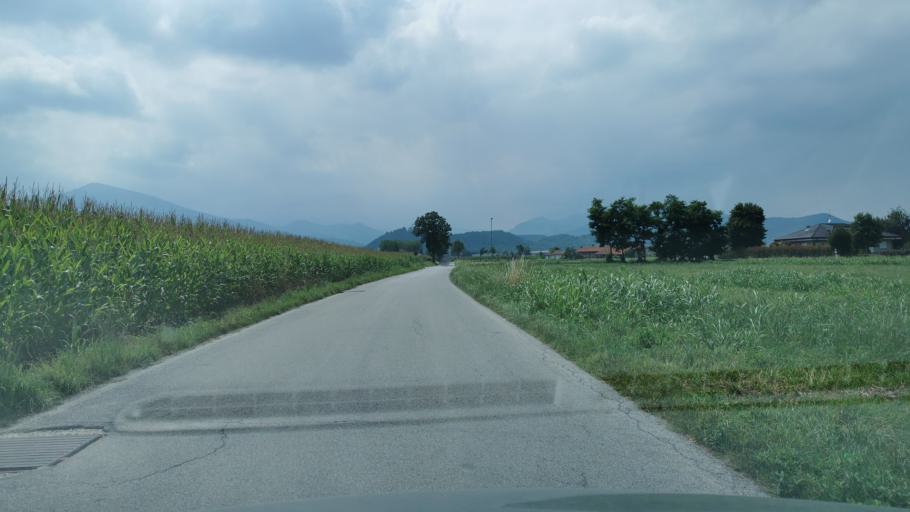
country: IT
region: Piedmont
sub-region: Provincia di Cuneo
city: Caraglio
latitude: 44.4243
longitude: 7.4548
